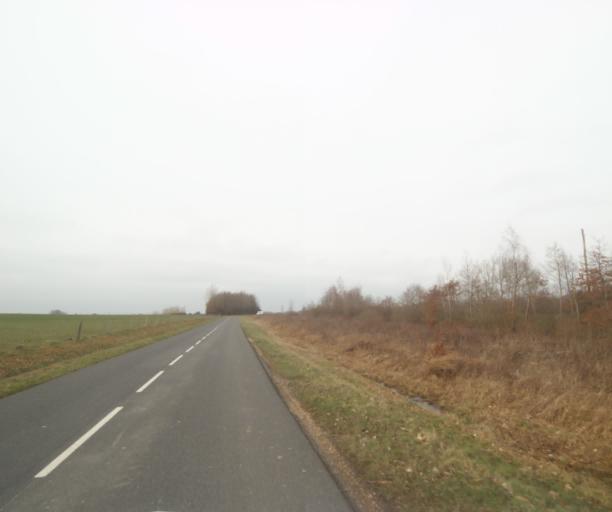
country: FR
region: Champagne-Ardenne
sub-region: Departement de la Marne
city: Pargny-sur-Saulx
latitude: 48.7411
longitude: 4.8638
